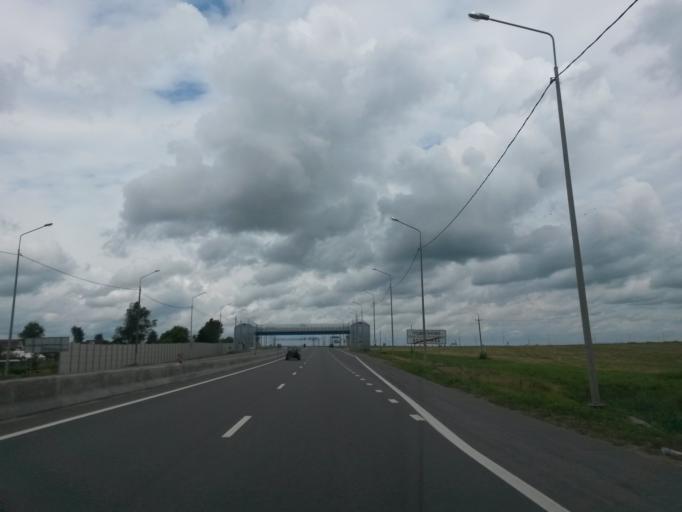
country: RU
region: Jaroslavl
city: Yaroslavl
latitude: 57.7160
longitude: 39.9030
